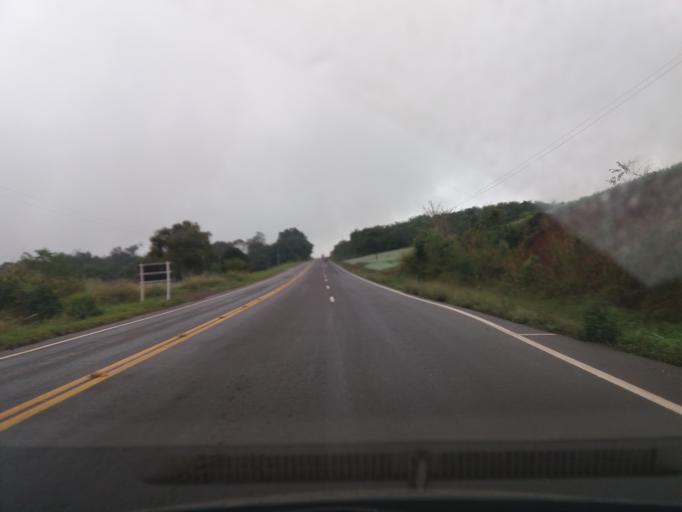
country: BR
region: Parana
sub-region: Realeza
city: Realeza
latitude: -25.5601
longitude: -53.5819
